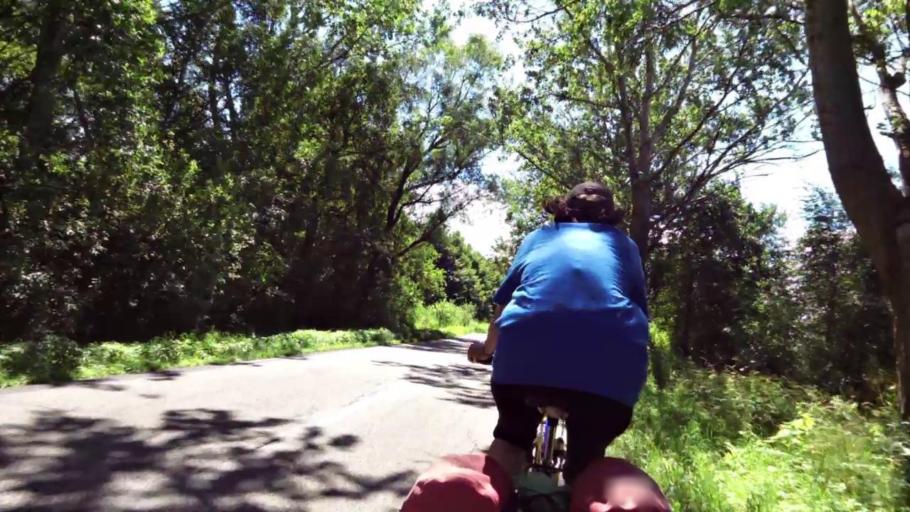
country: PL
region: West Pomeranian Voivodeship
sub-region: Koszalin
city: Koszalin
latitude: 54.2884
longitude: 16.2103
